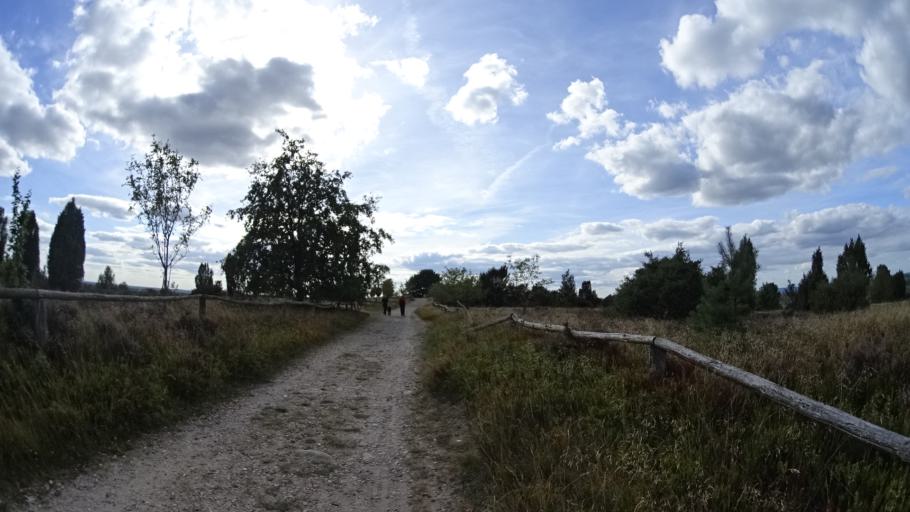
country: DE
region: Lower Saxony
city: Undeloh
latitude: 53.1675
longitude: 9.9418
